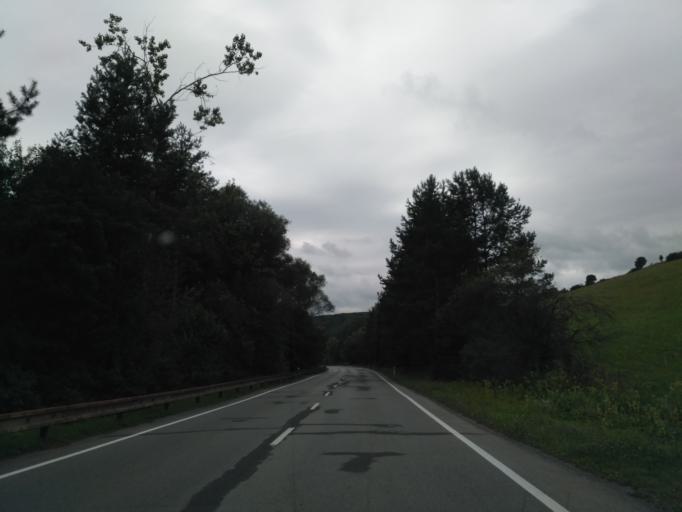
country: SK
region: Presovsky
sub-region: Okres Presov
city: Presov
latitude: 48.9618
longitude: 21.1652
